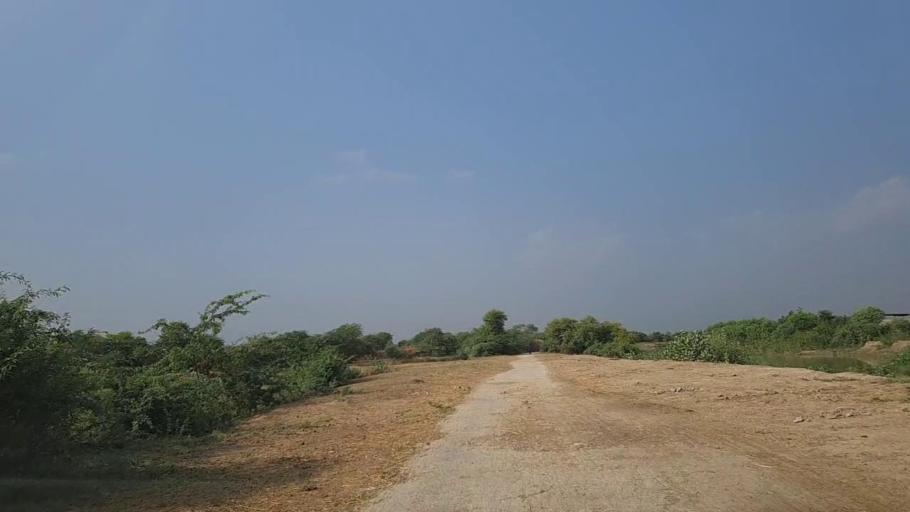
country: PK
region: Sindh
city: Daro Mehar
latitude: 24.7254
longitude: 68.1559
